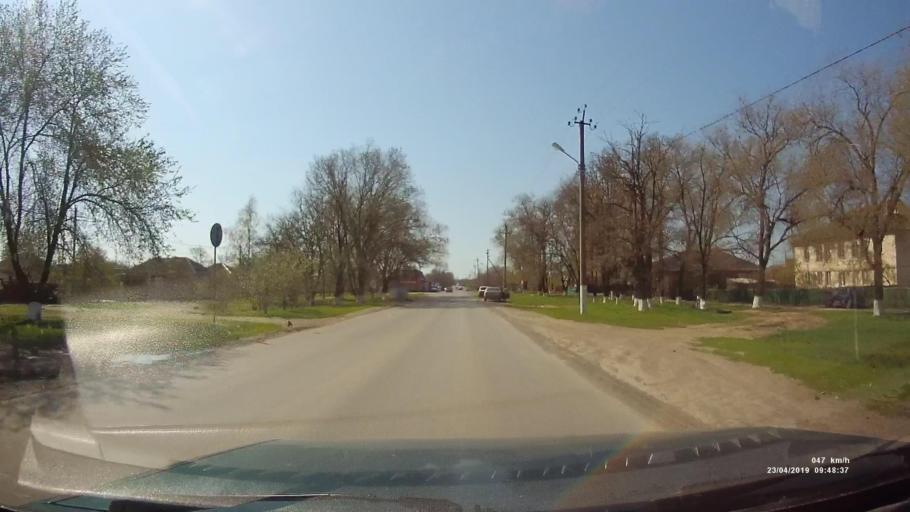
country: RU
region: Rostov
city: Orlovskiy
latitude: 46.8698
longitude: 42.0343
